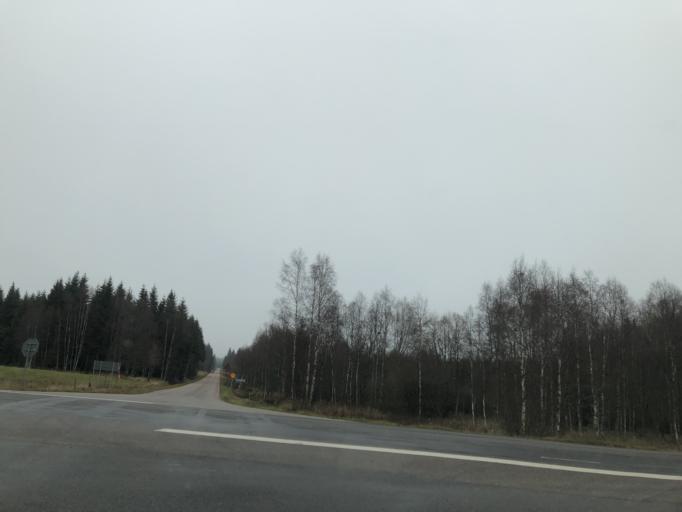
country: SE
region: Vaestra Goetaland
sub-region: Ulricehamns Kommun
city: Ulricehamn
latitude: 57.7254
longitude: 13.5489
